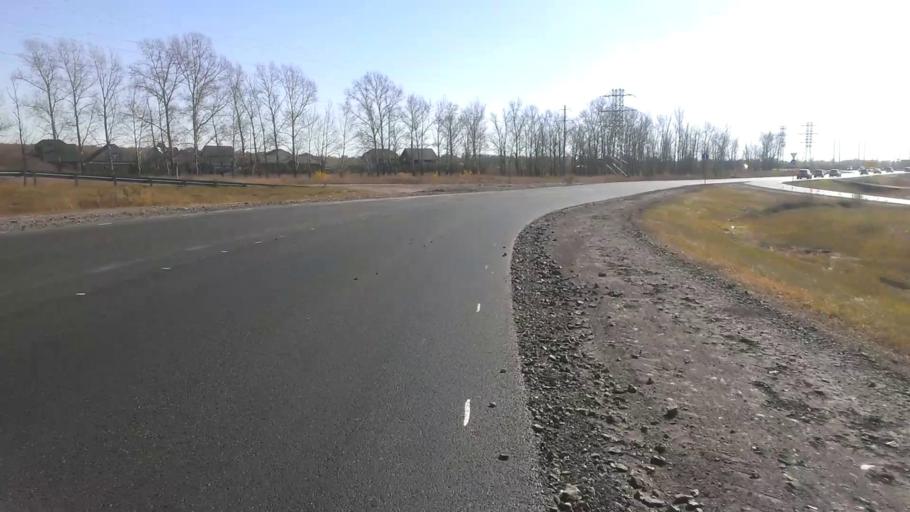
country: RU
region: Altai Krai
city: Sannikovo
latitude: 53.3397
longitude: 83.9381
